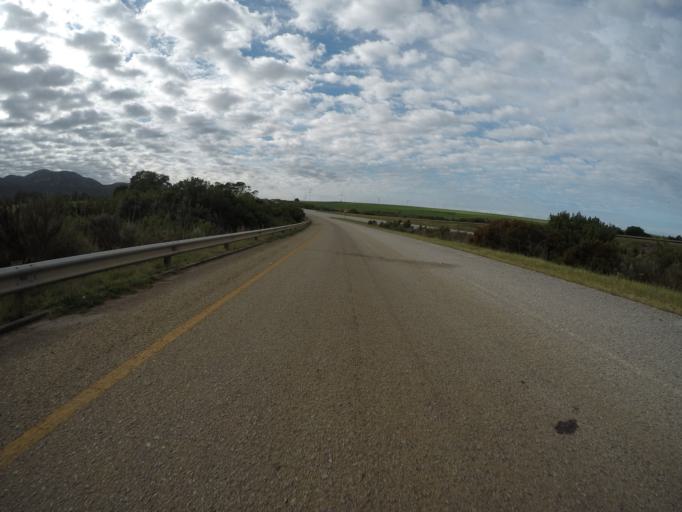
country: ZA
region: Eastern Cape
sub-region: Cacadu District Municipality
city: Kareedouw
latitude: -34.0504
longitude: 24.4574
